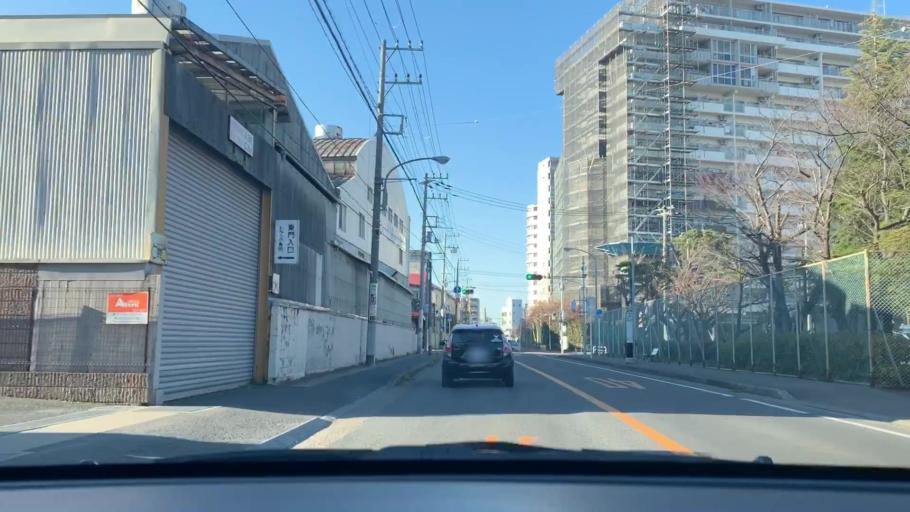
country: JP
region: Tokyo
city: Urayasu
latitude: 35.7219
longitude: 139.9063
